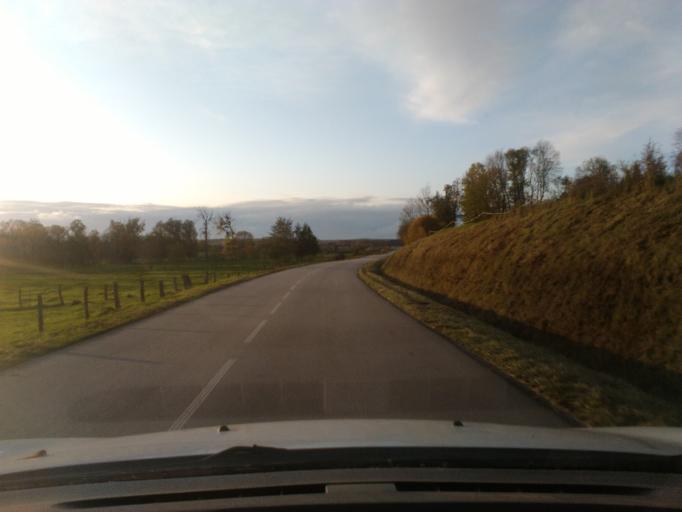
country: FR
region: Lorraine
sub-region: Departement des Vosges
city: Mirecourt
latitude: 48.2584
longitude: 6.1822
